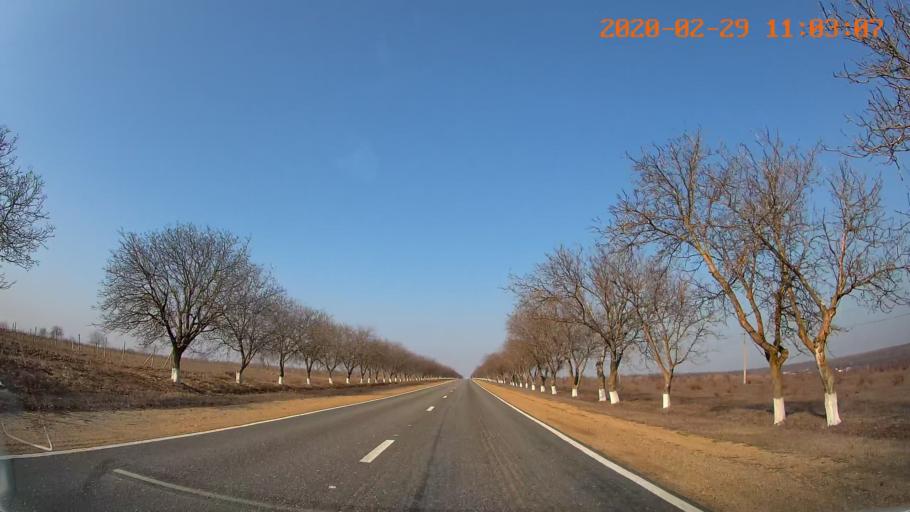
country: MD
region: Criuleni
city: Criuleni
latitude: 47.1772
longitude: 29.2245
